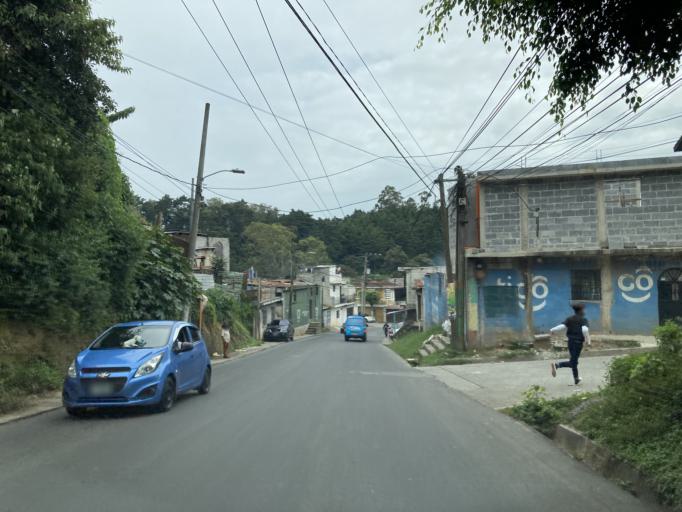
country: GT
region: Guatemala
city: San Jose Pinula
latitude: 14.5380
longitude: -90.4069
